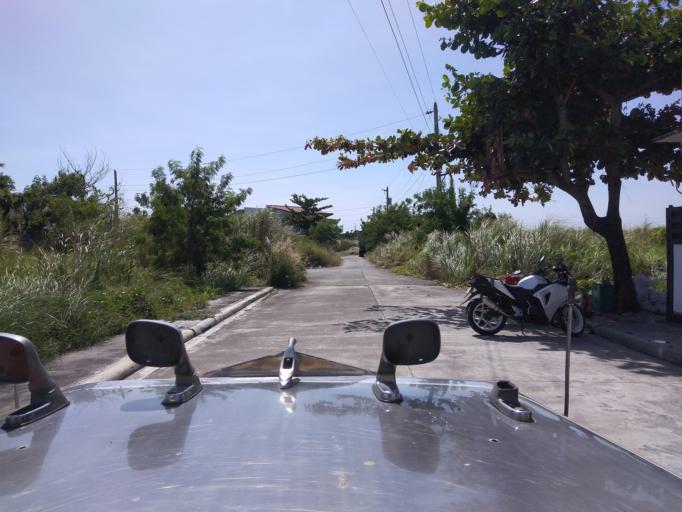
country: PH
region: Central Luzon
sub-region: Province of Pampanga
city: San Juan
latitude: 15.0179
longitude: 120.6707
